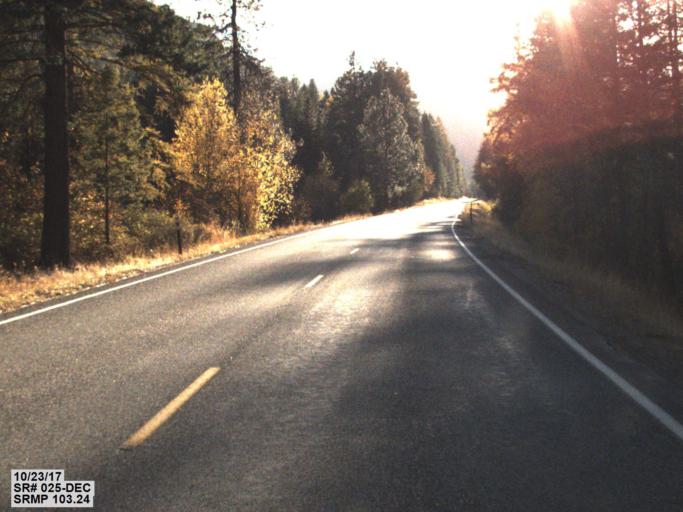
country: US
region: Washington
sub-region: Stevens County
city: Kettle Falls
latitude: 48.8191
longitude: -117.9209
